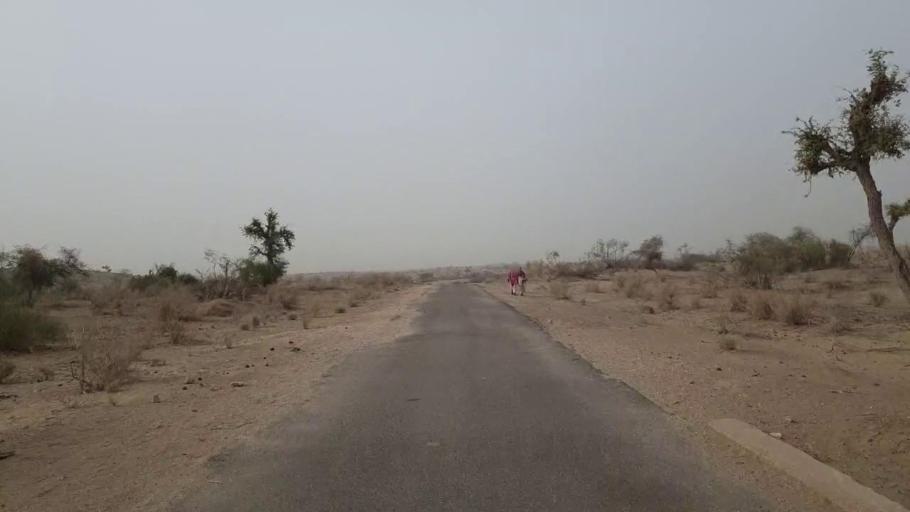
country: PK
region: Sindh
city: Islamkot
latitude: 24.5693
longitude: 70.3640
